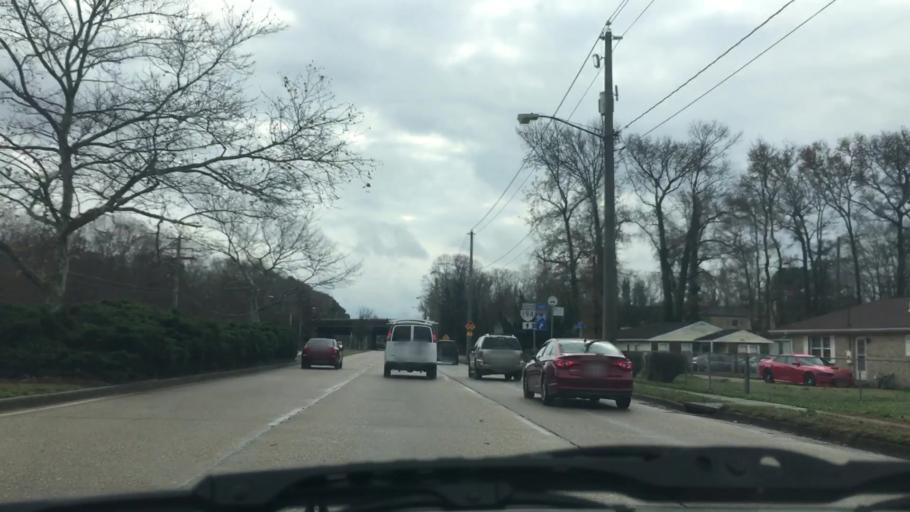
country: US
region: Virginia
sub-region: City of Norfolk
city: Norfolk
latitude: 36.9055
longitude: -76.2401
